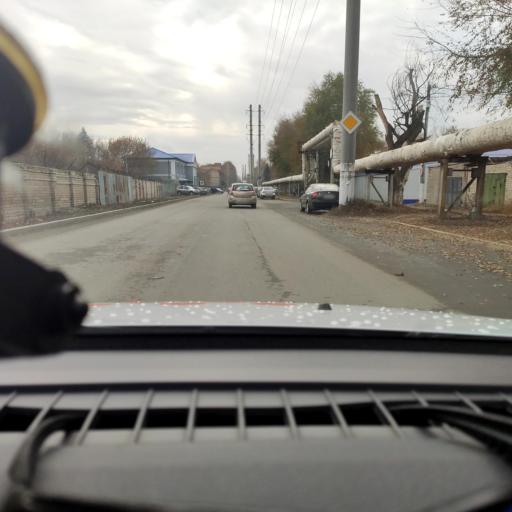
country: RU
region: Samara
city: Chapayevsk
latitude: 52.9801
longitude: 49.7202
